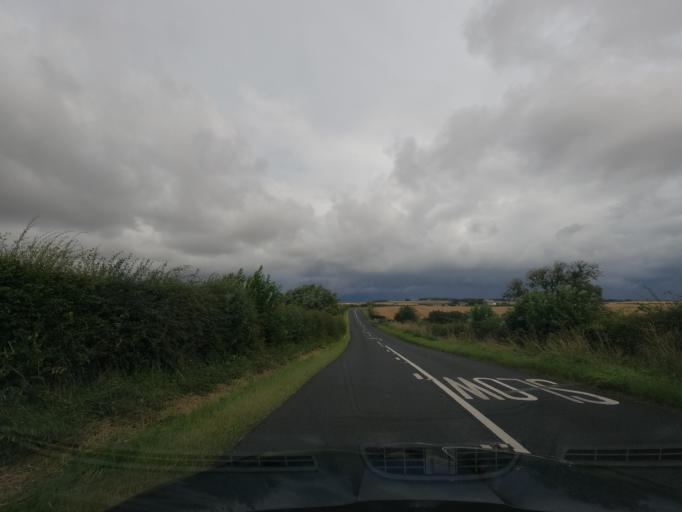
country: GB
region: England
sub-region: Northumberland
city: Ancroft
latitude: 55.7023
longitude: -2.0004
